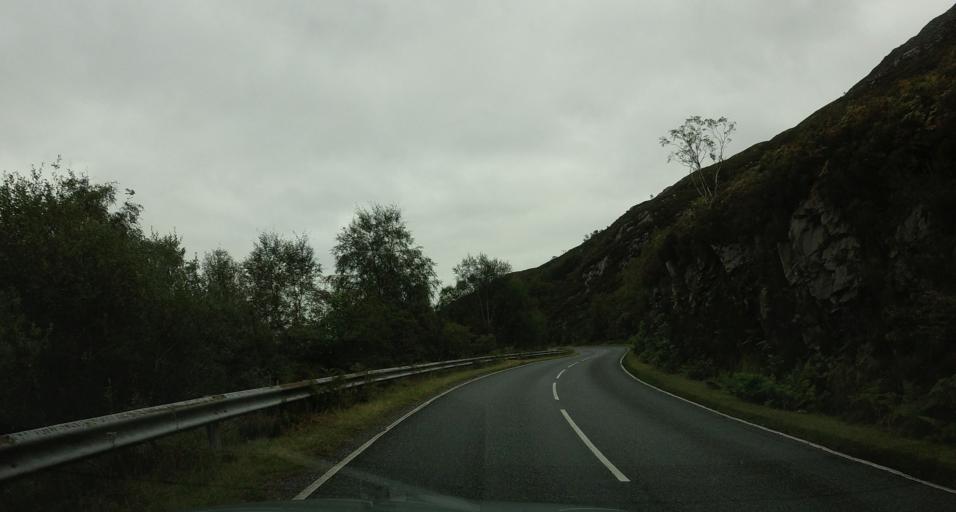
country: GB
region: Scotland
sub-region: Highland
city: Fort William
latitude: 56.6975
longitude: -5.0737
